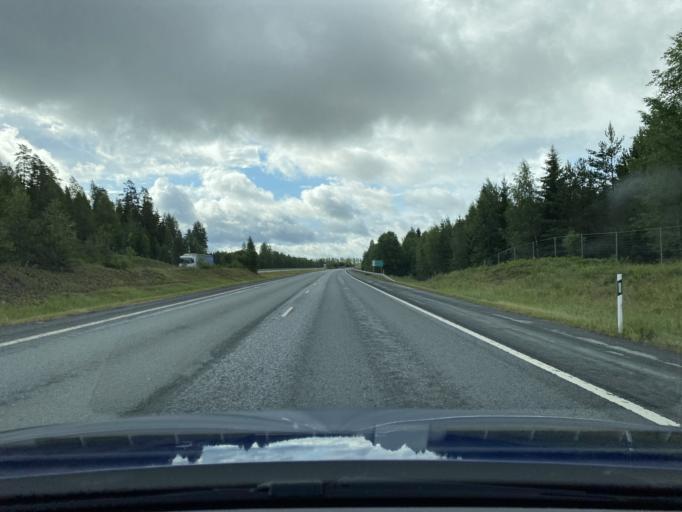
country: FI
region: Haeme
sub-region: Haemeenlinna
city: Kalvola
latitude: 61.1289
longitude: 24.1078
